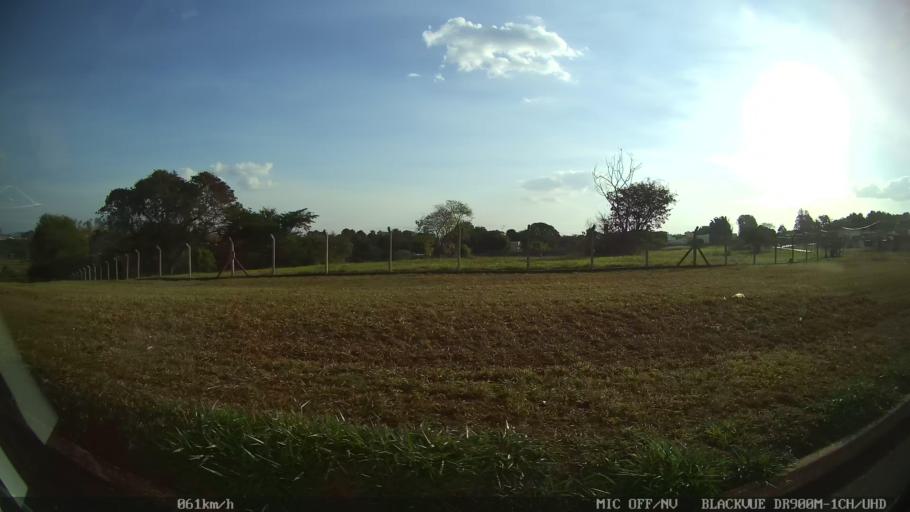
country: BR
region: Sao Paulo
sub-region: Ribeirao Preto
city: Ribeirao Preto
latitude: -21.1702
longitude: -47.8437
